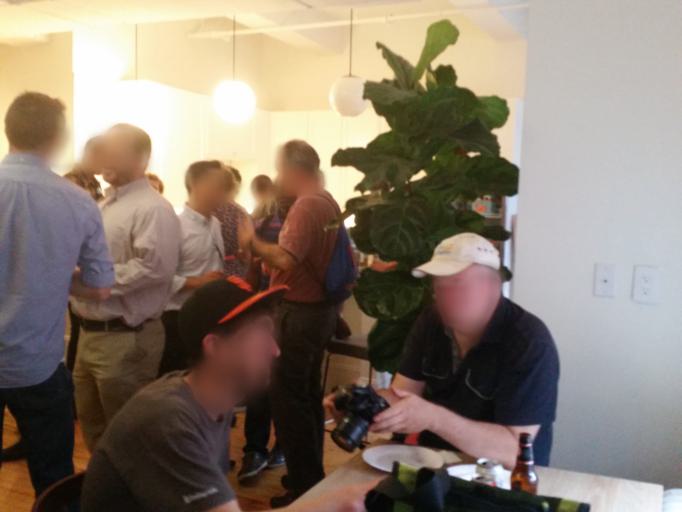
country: US
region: New York
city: New York City
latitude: 40.7433
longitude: -73.9906
